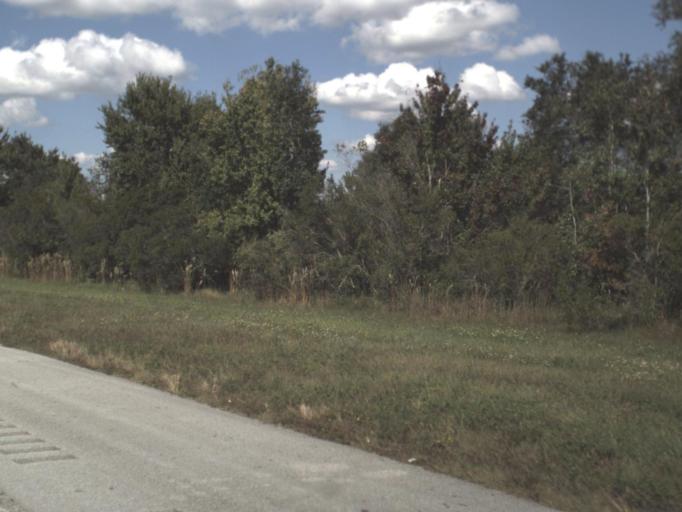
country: US
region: Florida
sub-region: Brevard County
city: June Park
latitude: 27.8694
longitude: -81.0171
